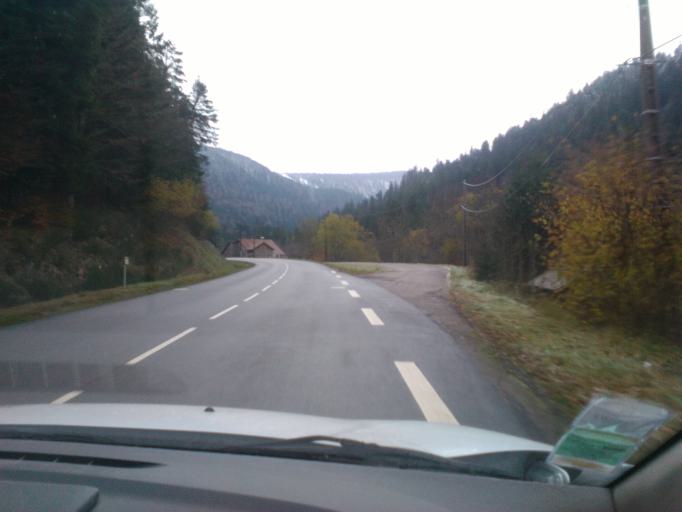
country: FR
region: Lorraine
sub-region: Departement des Vosges
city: Xonrupt-Longemer
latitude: 48.0623
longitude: 6.9703
